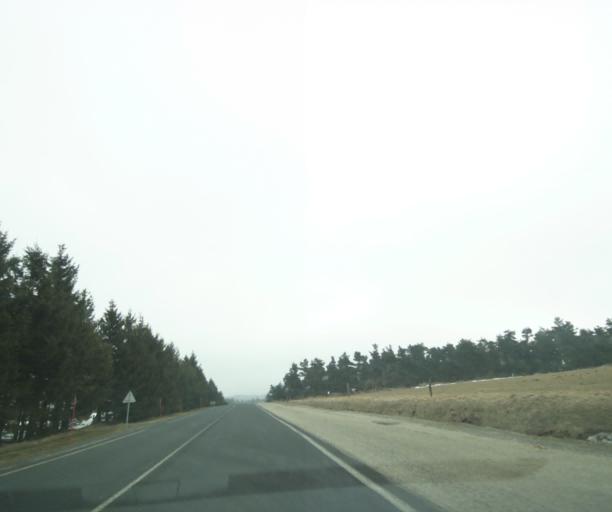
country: FR
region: Languedoc-Roussillon
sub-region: Departement de la Lozere
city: Langogne
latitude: 44.7557
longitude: 3.9648
